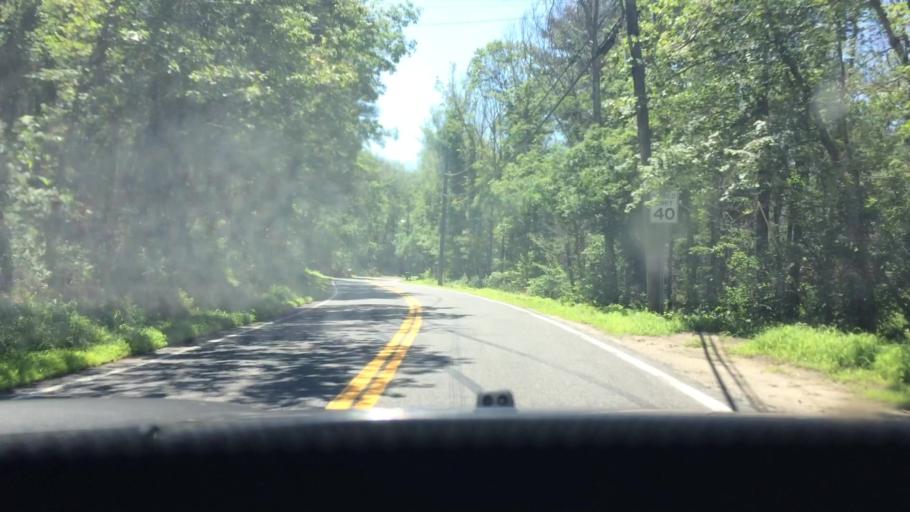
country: US
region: Rhode Island
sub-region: Providence County
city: Harrisville
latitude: 42.0031
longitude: -71.6810
